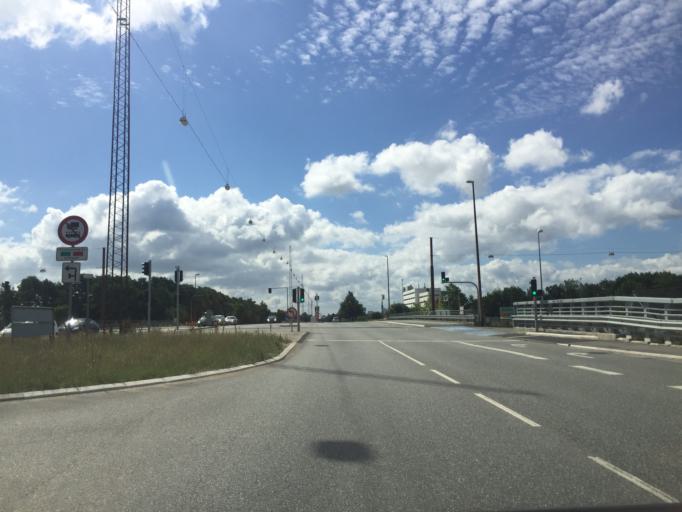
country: DK
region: Capital Region
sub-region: Hvidovre Kommune
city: Hvidovre
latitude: 55.6497
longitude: 12.4583
